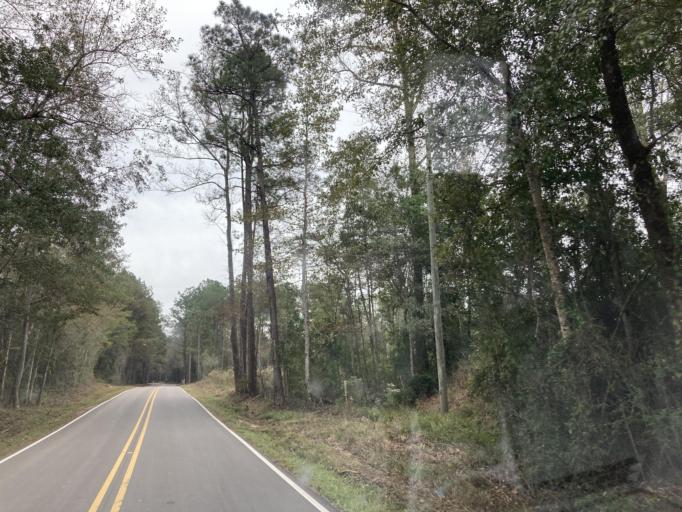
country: US
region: Mississippi
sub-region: Lamar County
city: Purvis
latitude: 31.1099
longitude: -89.4261
